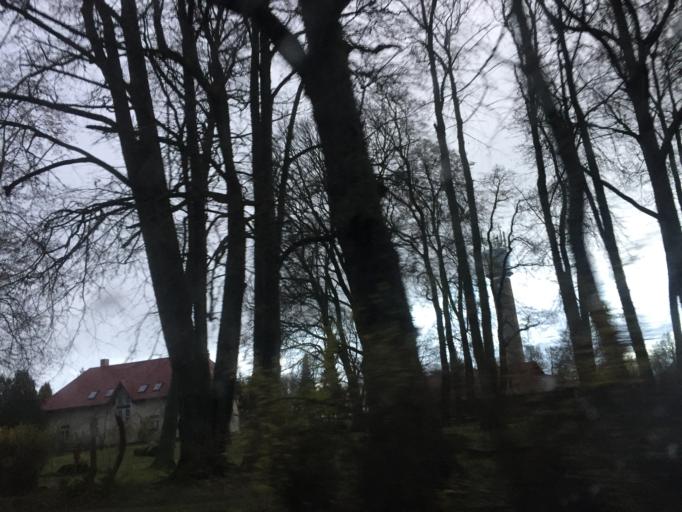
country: LV
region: Burtnieki
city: Matisi
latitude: 57.6959
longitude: 25.2735
